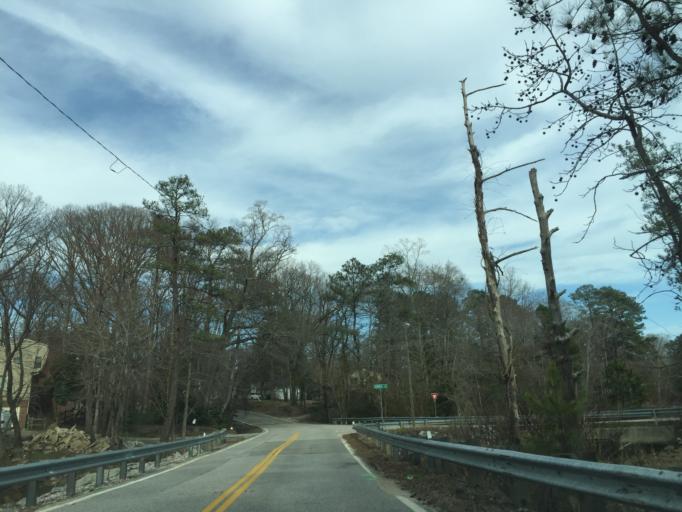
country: US
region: Virginia
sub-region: City of Newport News
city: Newport News
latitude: 37.0845
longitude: -76.5129
